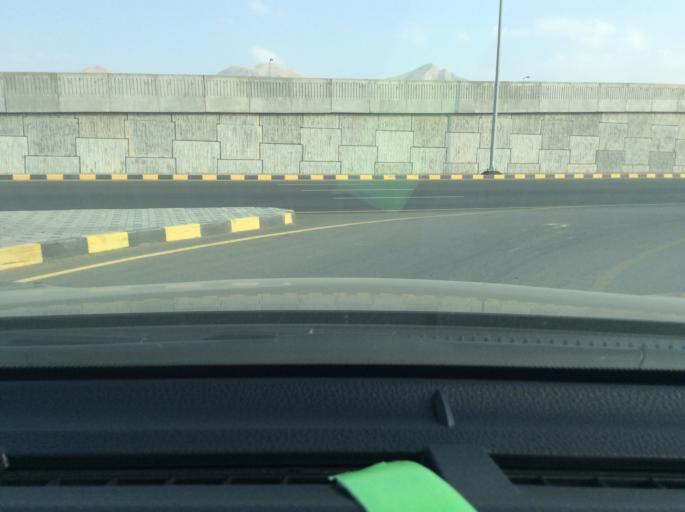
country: OM
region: Muhafazat Masqat
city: Bawshar
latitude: 23.5063
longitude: 58.5000
